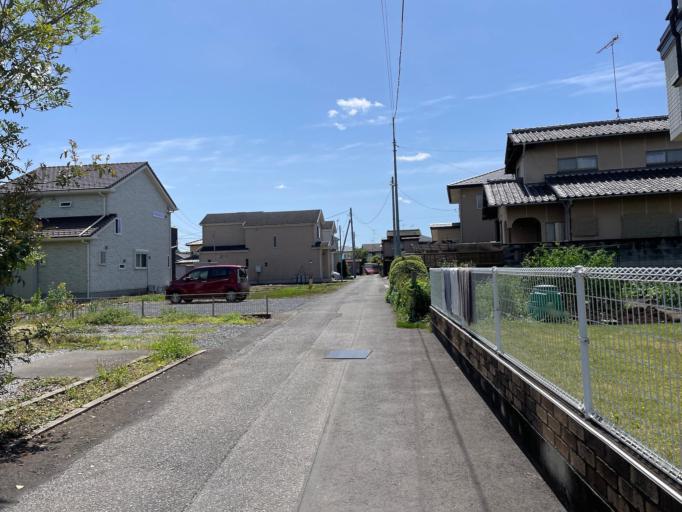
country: JP
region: Tochigi
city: Sano
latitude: 36.3251
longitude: 139.5860
